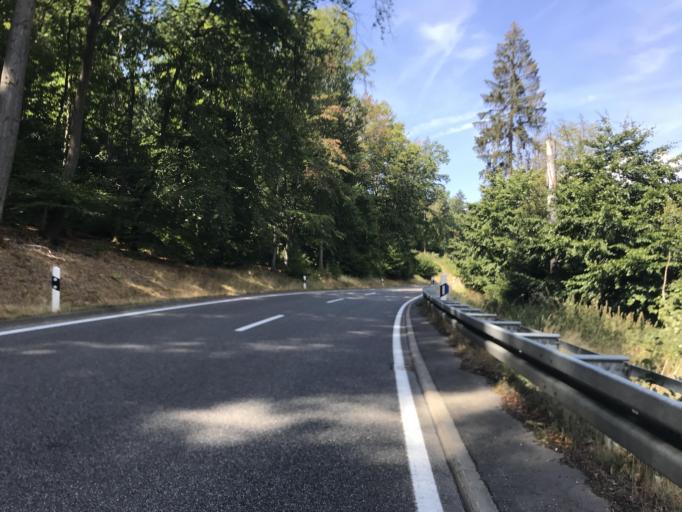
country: DE
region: Hesse
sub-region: Regierungsbezirk Darmstadt
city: Kiedrich
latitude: 50.0722
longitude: 8.0544
